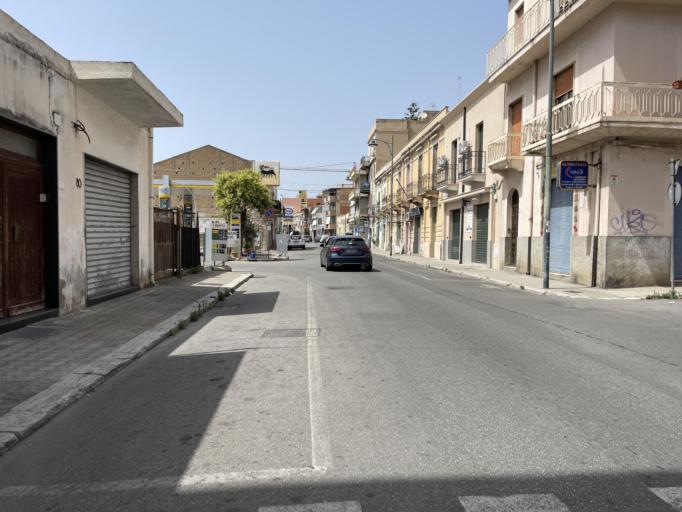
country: IT
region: Calabria
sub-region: Provincia di Reggio Calabria
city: Reggio Calabria
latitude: 38.0988
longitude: 15.6429
